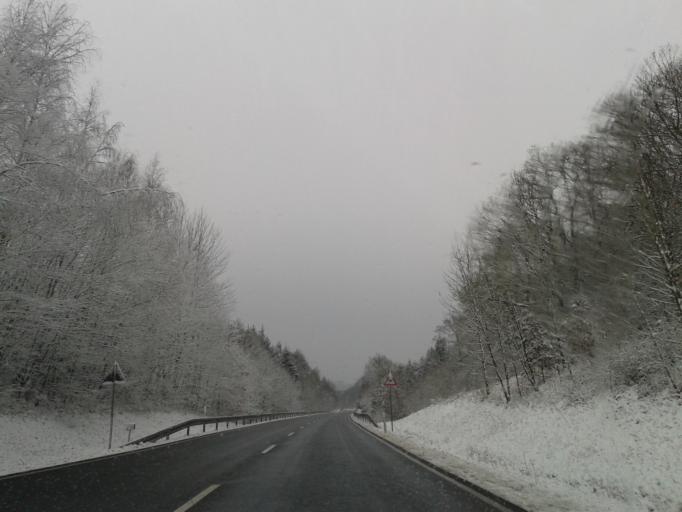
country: DE
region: Bavaria
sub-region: Regierungsbezirk Unterfranken
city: Gadheim
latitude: 50.0360
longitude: 10.3501
